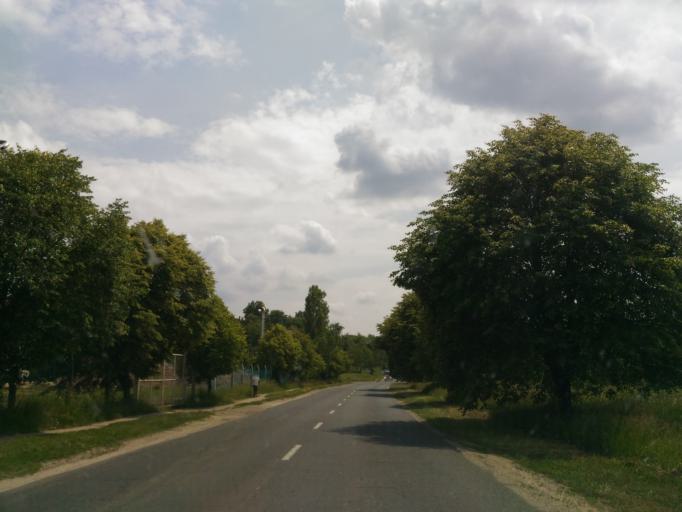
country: HU
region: Baranya
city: Komlo
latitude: 46.1993
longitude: 18.2521
